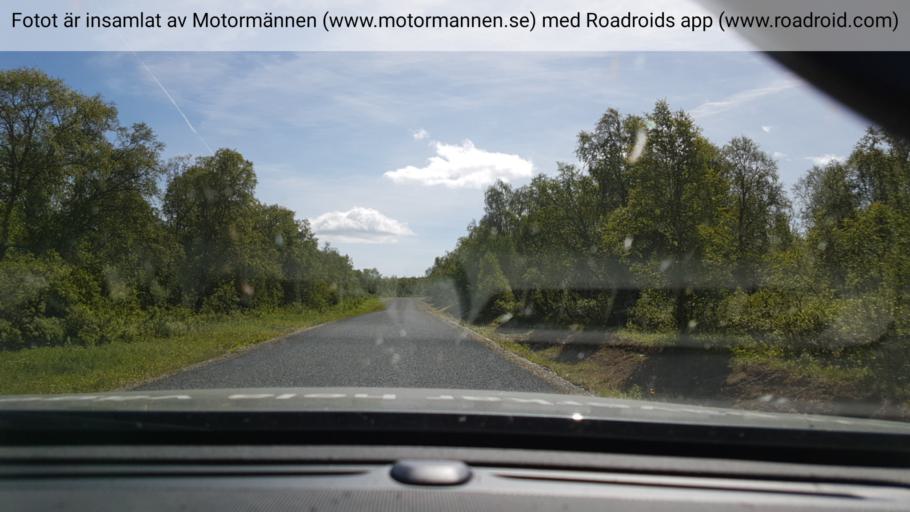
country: NO
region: Nordland
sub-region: Hattfjelldal
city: Hattfjelldal
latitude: 65.4189
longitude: 14.9200
